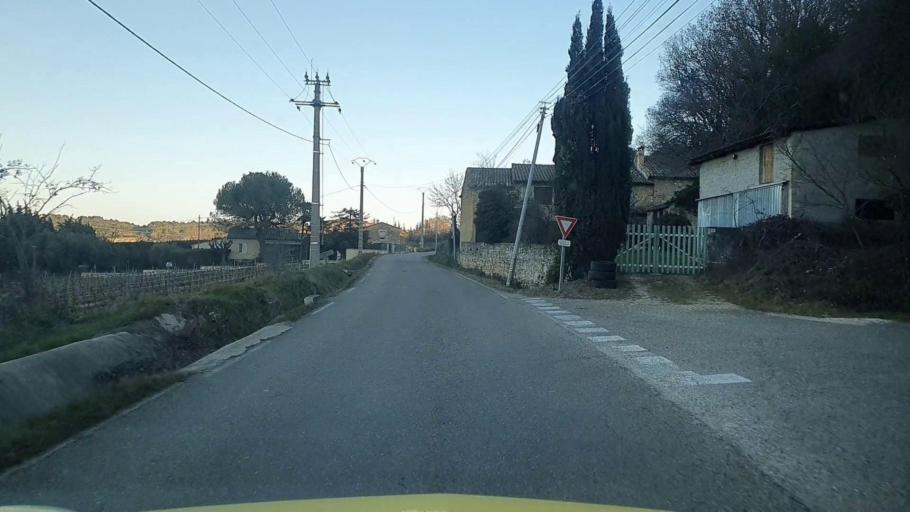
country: FR
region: Languedoc-Roussillon
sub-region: Departement du Gard
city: Venejan
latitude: 44.2000
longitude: 4.6580
